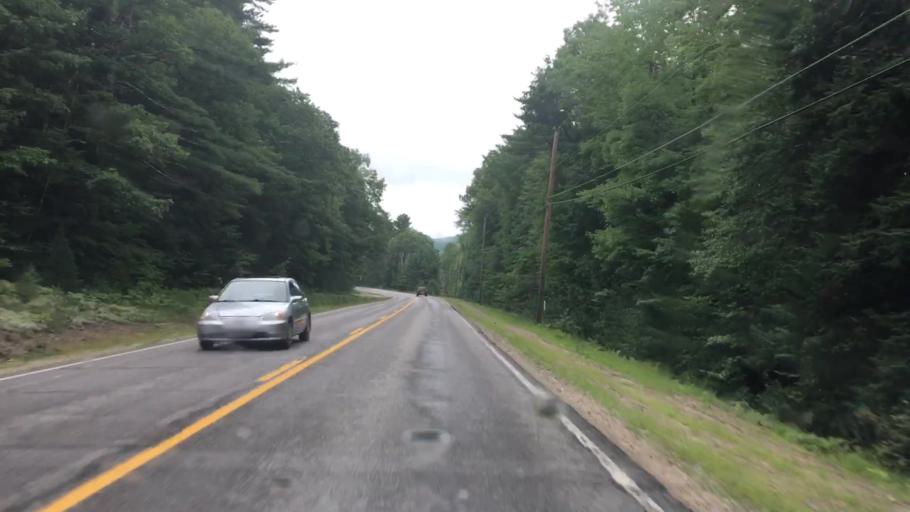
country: US
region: Maine
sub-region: Oxford County
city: Fryeburg
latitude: 43.9918
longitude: -70.9368
